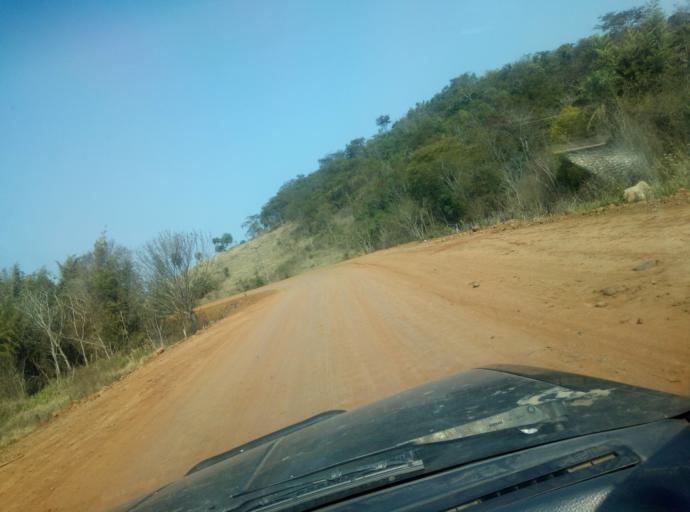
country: PY
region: Caaguazu
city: Coronel Oviedo
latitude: -25.3384
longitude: -56.3154
